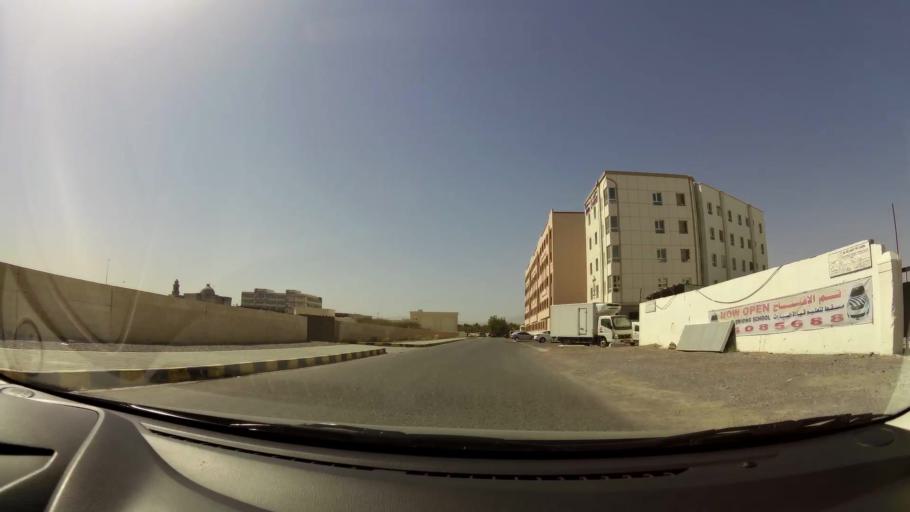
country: OM
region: Muhafazat Masqat
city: As Sib al Jadidah
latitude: 23.6104
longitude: 58.2438
